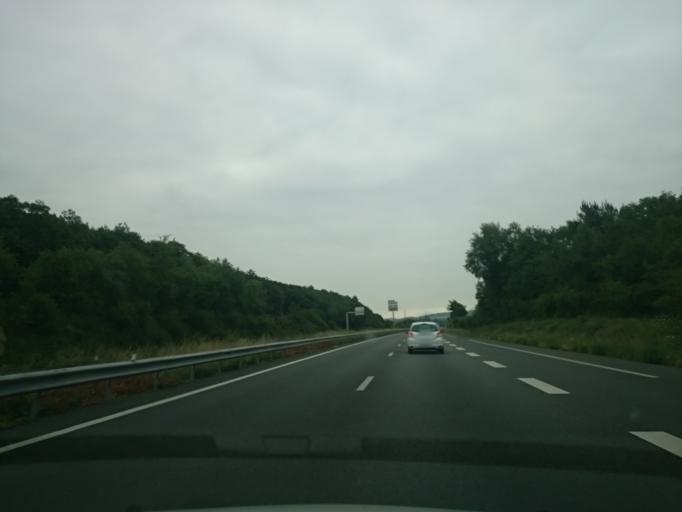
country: FR
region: Brittany
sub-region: Departement du Finistere
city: Le Faou
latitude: 48.2948
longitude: -4.1679
